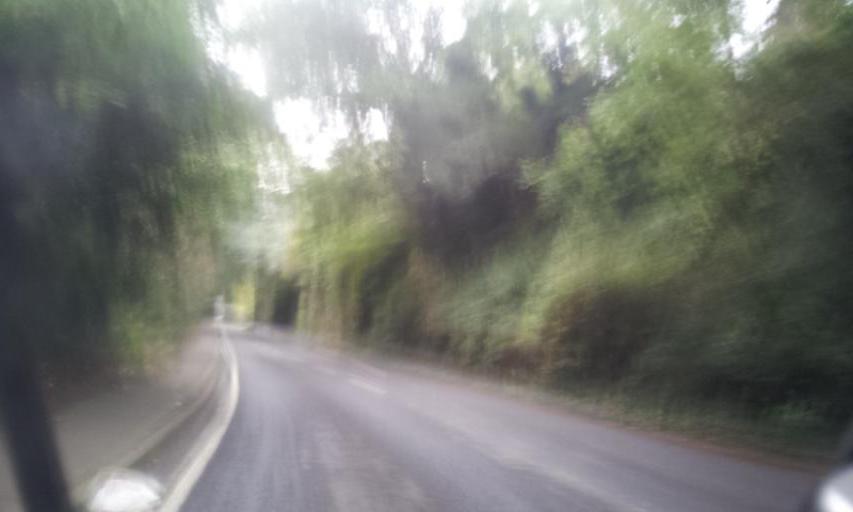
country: GB
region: England
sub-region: Kent
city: Larkfield
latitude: 51.2784
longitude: 0.4361
